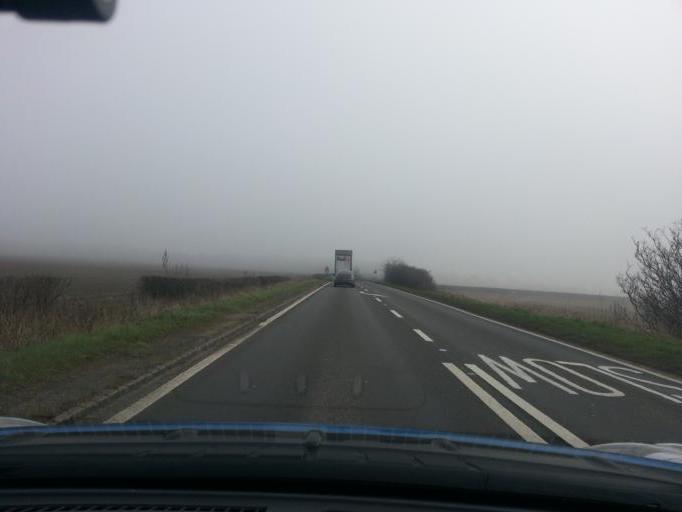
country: GB
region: England
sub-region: Oxfordshire
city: Stanford in the Vale
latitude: 51.6745
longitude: -1.5250
